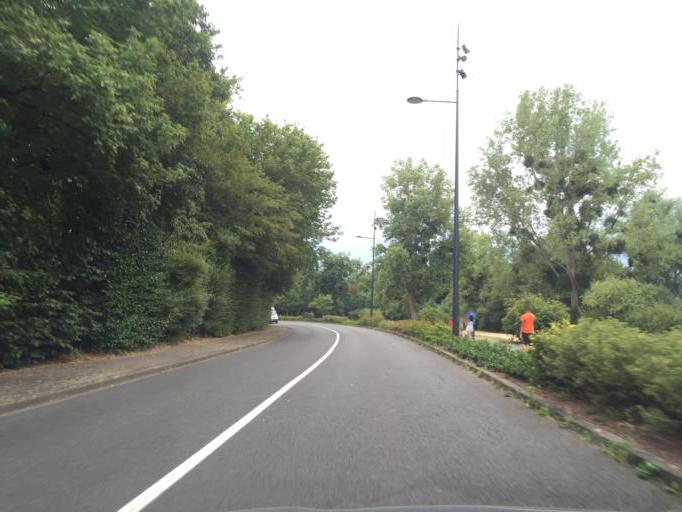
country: FR
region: Auvergne
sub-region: Departement de l'Allier
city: Moulins
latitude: 46.5395
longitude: 3.3327
